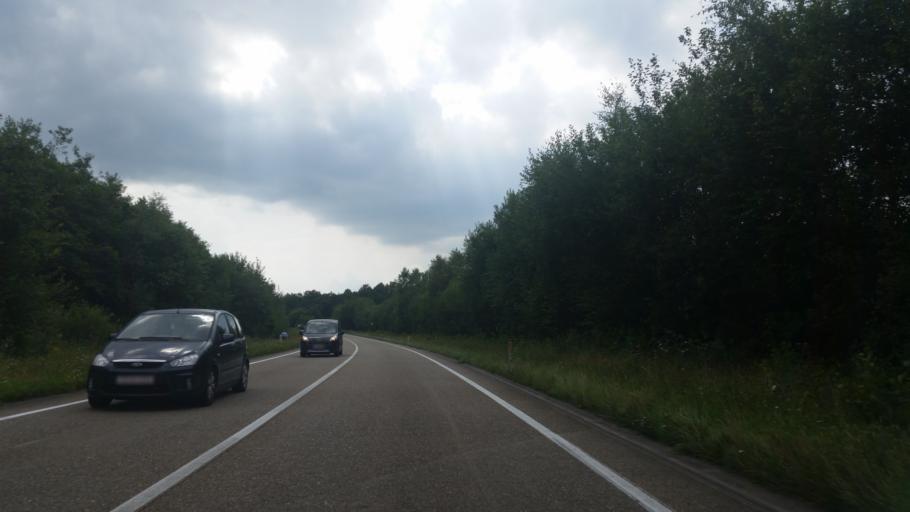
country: BE
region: Flanders
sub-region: Provincie Antwerpen
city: Kasterlee
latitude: 51.2479
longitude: 4.9567
